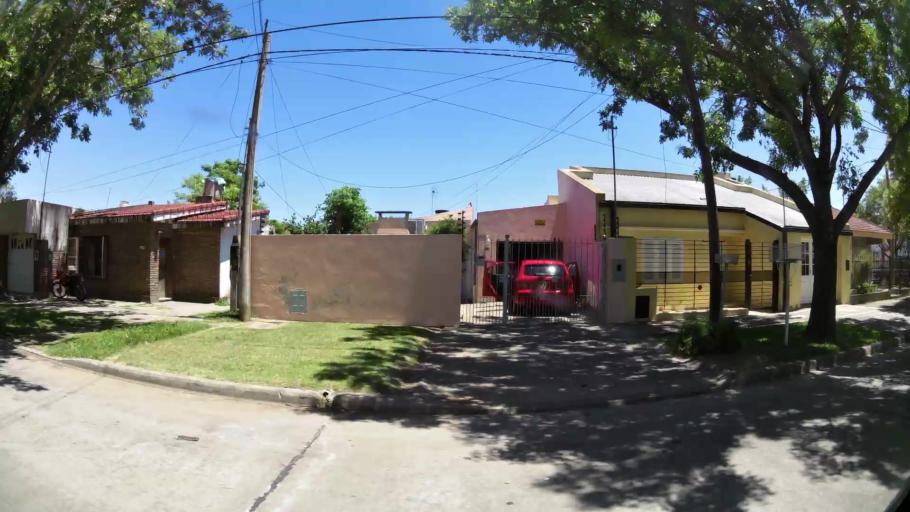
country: AR
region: Santa Fe
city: Rafaela
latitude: -31.2506
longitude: -61.4598
